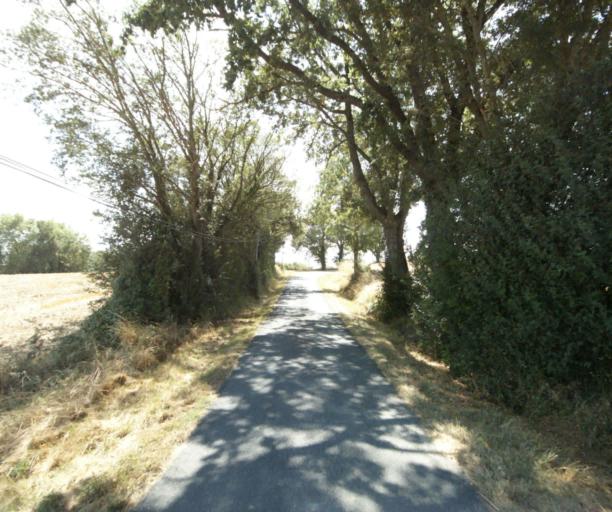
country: FR
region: Midi-Pyrenees
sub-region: Departement du Tarn
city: Puylaurens
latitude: 43.5310
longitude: 2.0114
